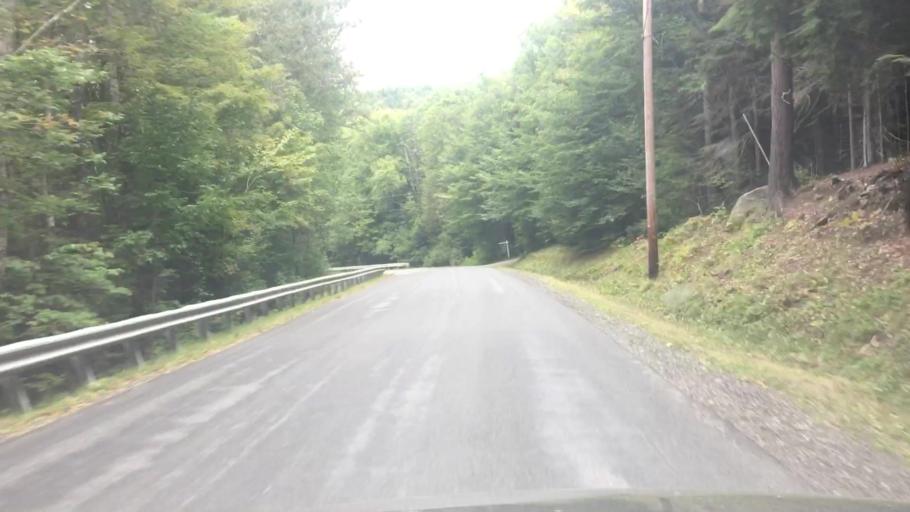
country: US
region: Vermont
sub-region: Windham County
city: Dover
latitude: 42.8446
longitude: -72.8302
